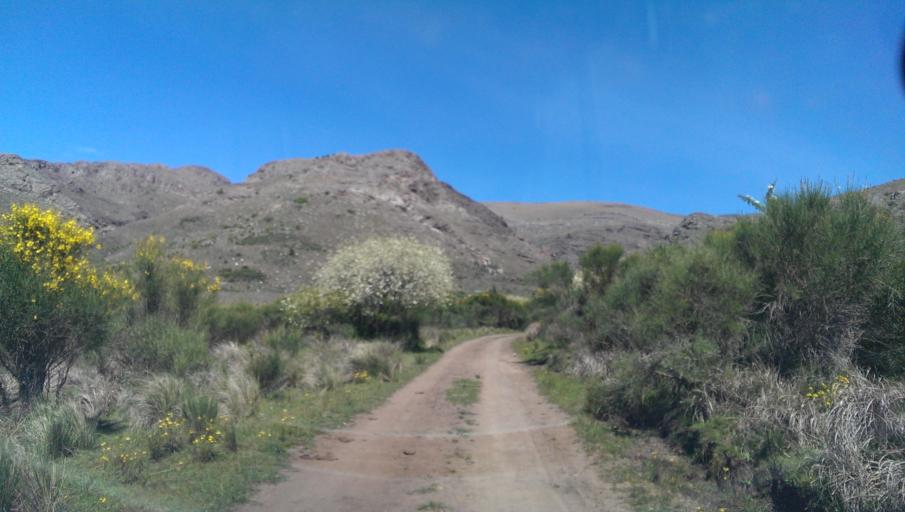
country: AR
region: Buenos Aires
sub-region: Partido de Tornquist
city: Tornquist
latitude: -38.1027
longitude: -61.9456
